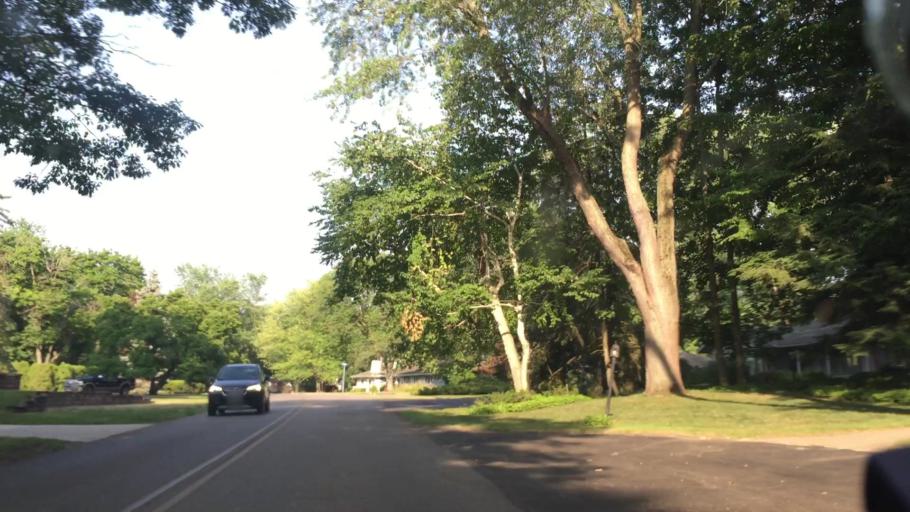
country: US
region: Michigan
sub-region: Oakland County
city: Beverly Hills
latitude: 42.5275
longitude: -83.2387
